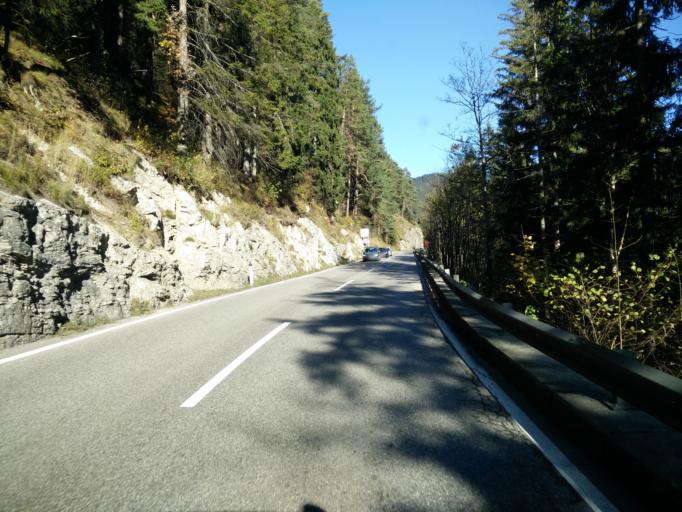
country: AT
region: Tyrol
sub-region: Politischer Bezirk Imst
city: Nassereith
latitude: 47.3465
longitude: 10.8203
